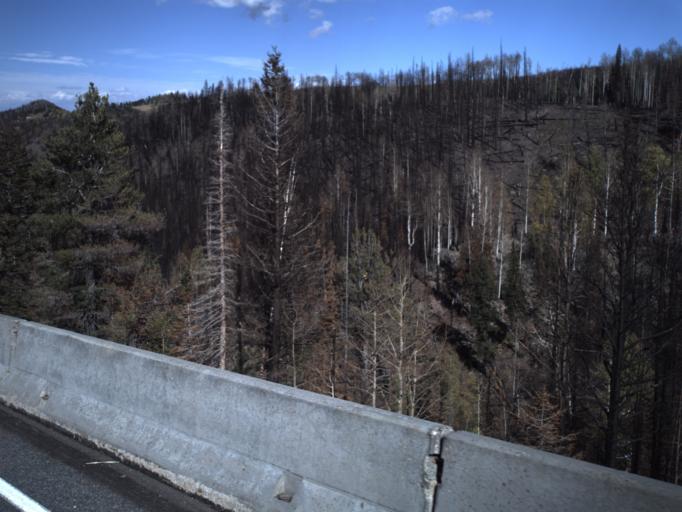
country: US
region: Utah
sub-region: Iron County
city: Parowan
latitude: 37.7146
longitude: -112.8485
